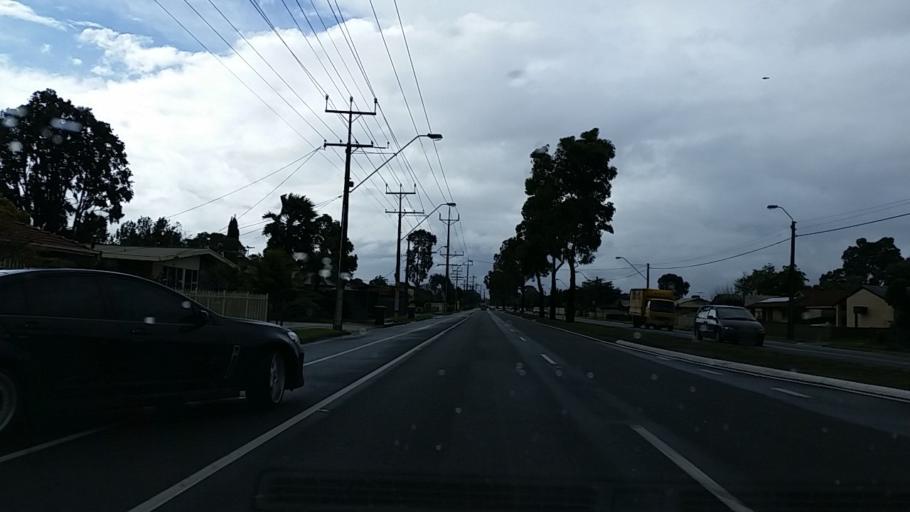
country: AU
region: South Australia
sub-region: Salisbury
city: Salisbury
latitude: -34.7748
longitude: 138.6302
